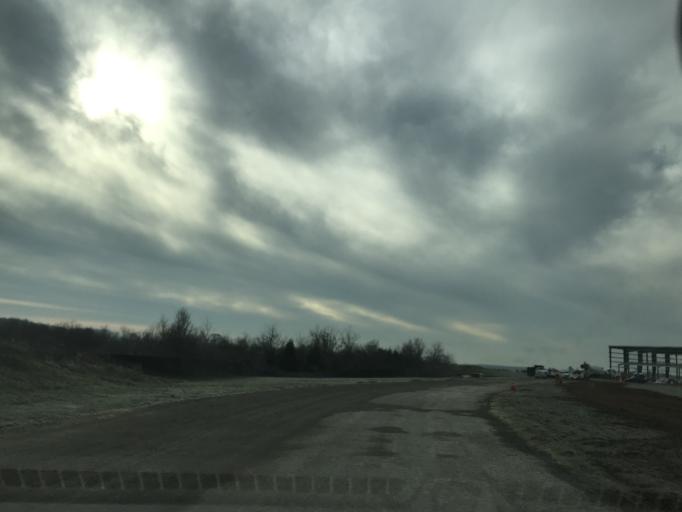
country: US
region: Virginia
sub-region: City of Manassas
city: Manassas
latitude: 38.7226
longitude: -77.5082
